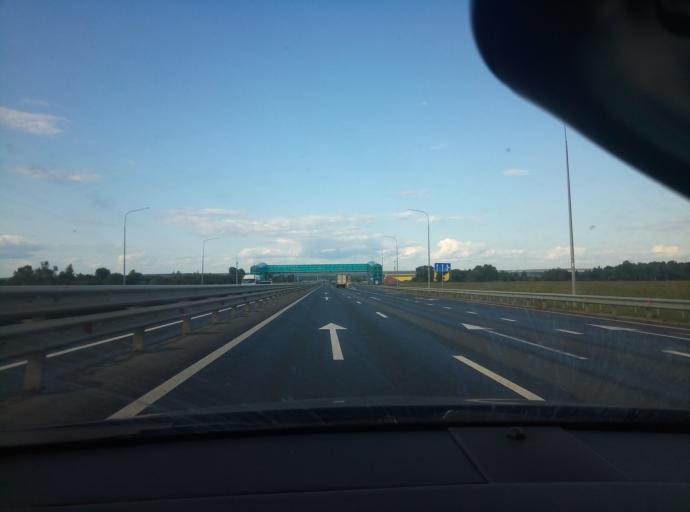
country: RU
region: Kaluga
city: Kurovskoye
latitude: 54.5380
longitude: 36.0028
